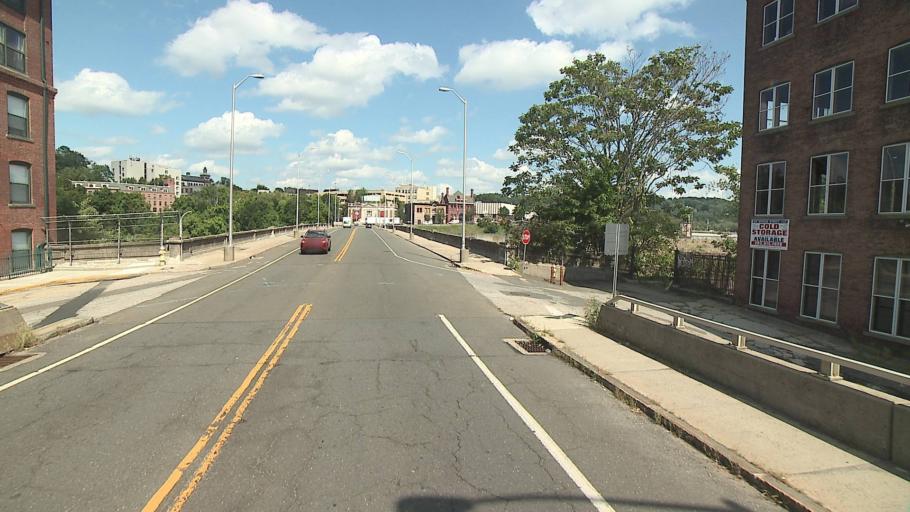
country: US
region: Connecticut
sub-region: Fairfield County
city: Shelton
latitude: 41.3186
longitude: -73.0920
